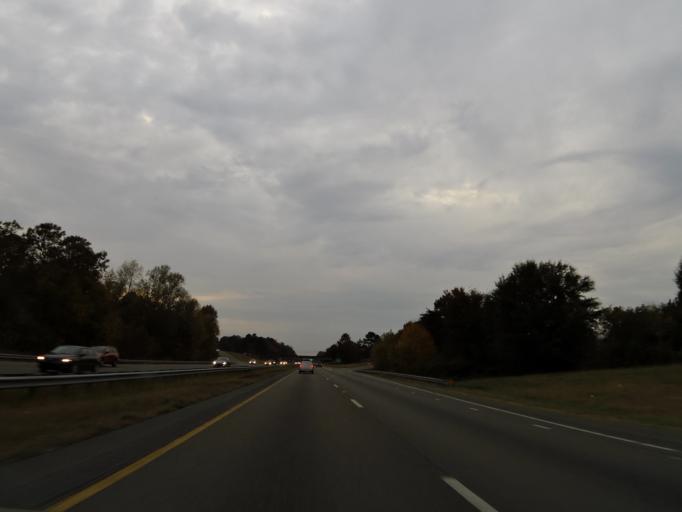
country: US
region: North Carolina
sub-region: Burke County
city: Hildebran
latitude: 35.7083
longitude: -81.4352
